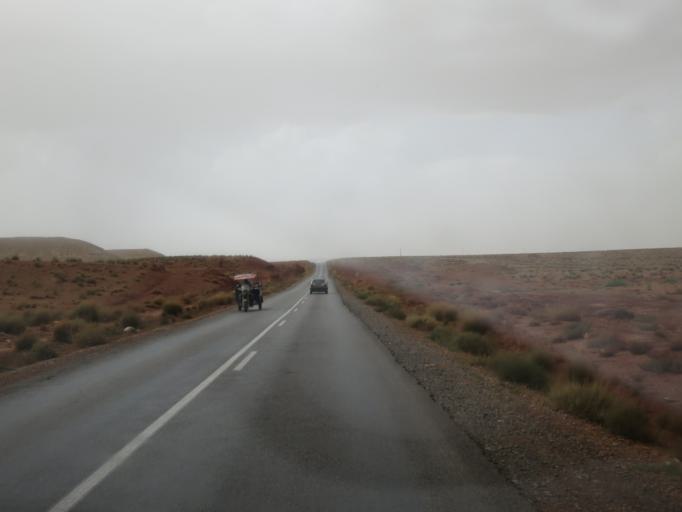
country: MA
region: Meknes-Tafilalet
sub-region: Khenifra
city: Itzer
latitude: 32.8539
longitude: -4.9474
